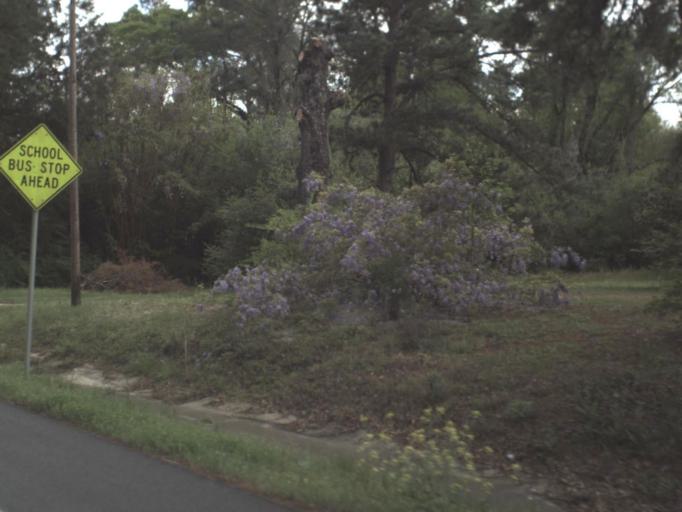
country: US
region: Alabama
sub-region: Covington County
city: Florala
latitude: 30.9678
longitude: -86.4474
